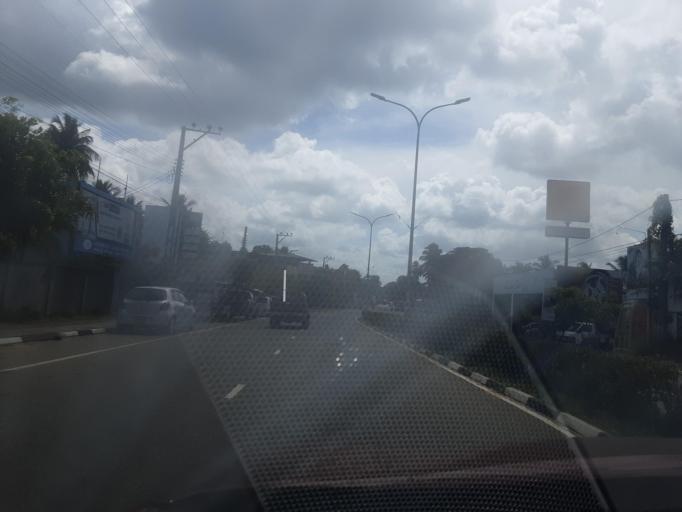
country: LK
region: North Western
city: Kuliyapitiya
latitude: 7.4704
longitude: 80.0450
